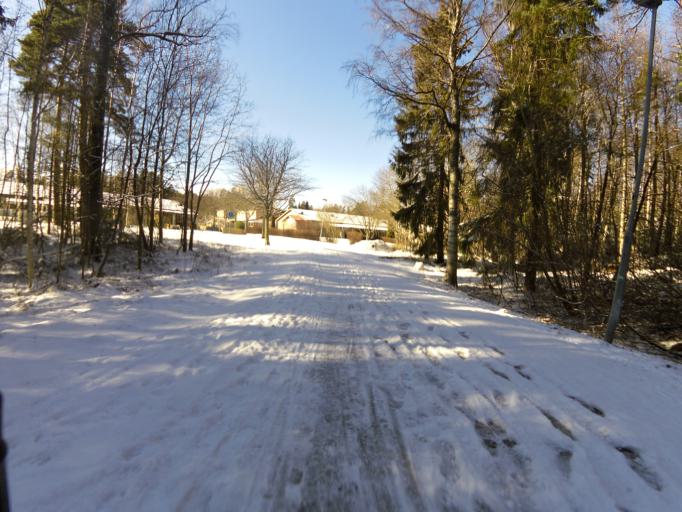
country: SE
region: Gaevleborg
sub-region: Gavle Kommun
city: Gavle
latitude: 60.6644
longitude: 17.2326
